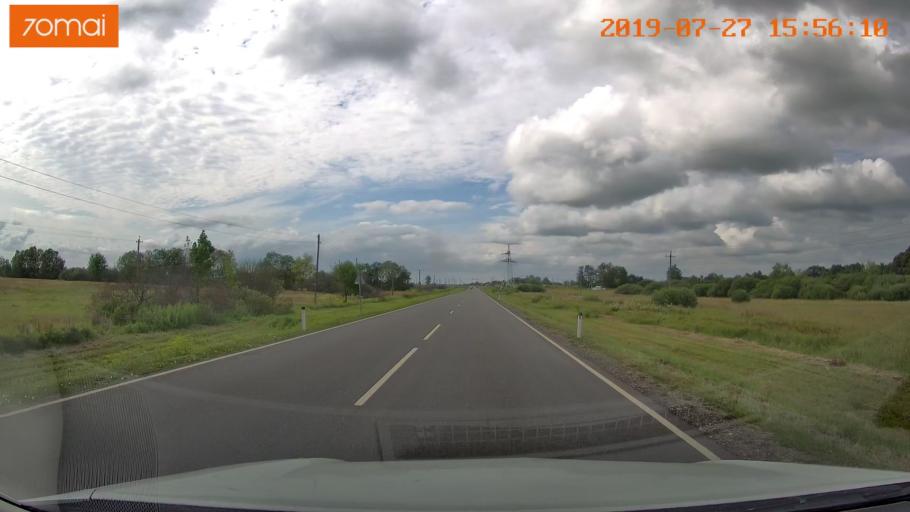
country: RU
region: Kaliningrad
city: Chernyakhovsk
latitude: 54.6173
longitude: 21.9068
